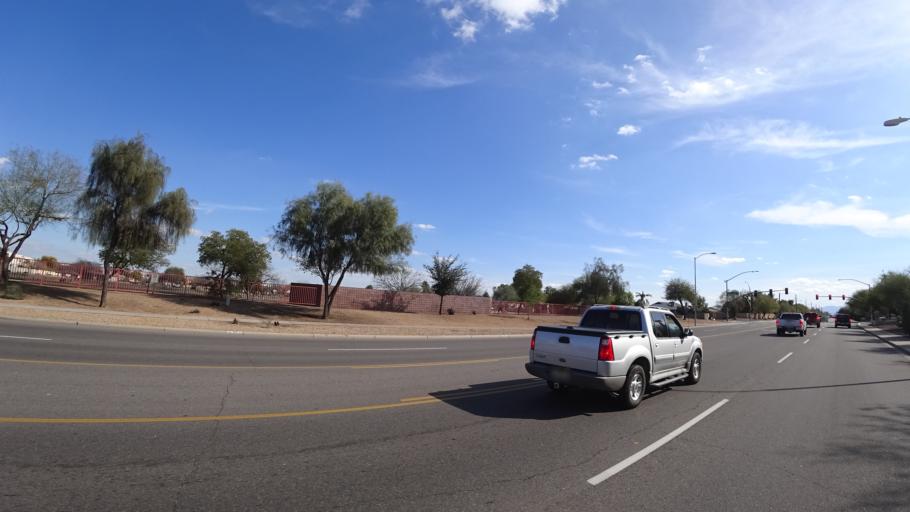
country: US
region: Arizona
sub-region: Maricopa County
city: Peoria
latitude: 33.6042
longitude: -112.2202
